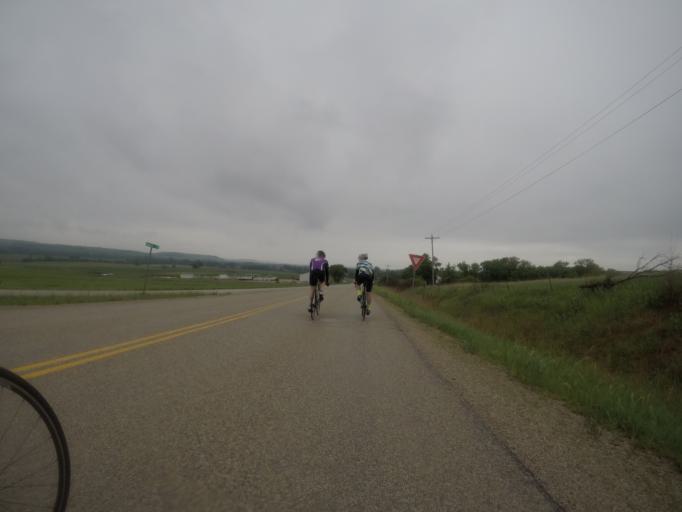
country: US
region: Kansas
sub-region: Pottawatomie County
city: Wamego
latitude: 39.3755
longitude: -96.2213
